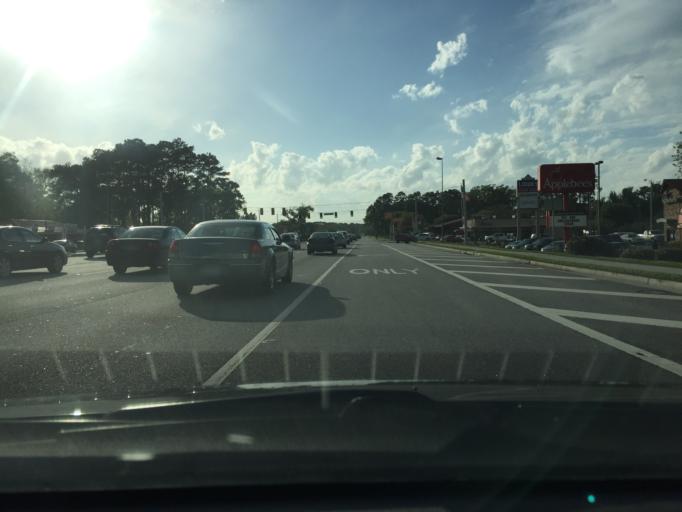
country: US
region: Georgia
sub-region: Chatham County
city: Montgomery
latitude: 31.9798
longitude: -81.1423
